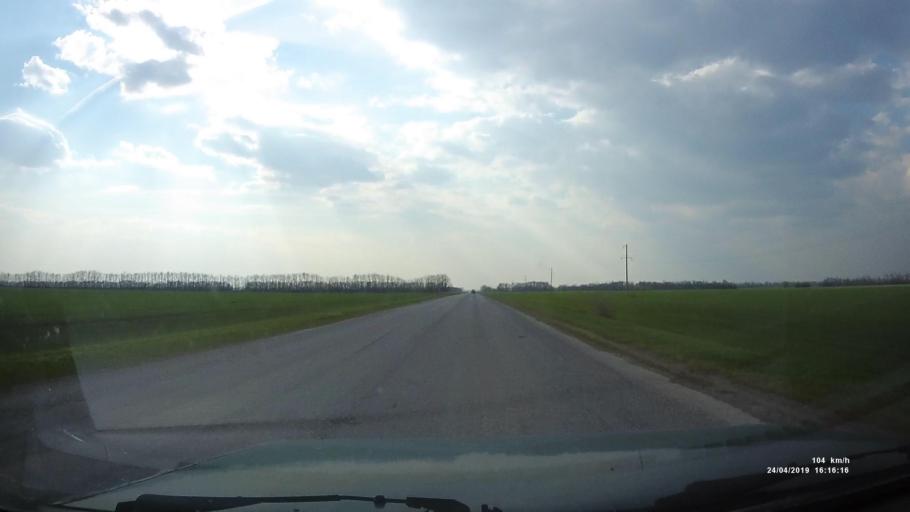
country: RU
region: Rostov
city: Sovetskoye
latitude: 46.7622
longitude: 42.1632
